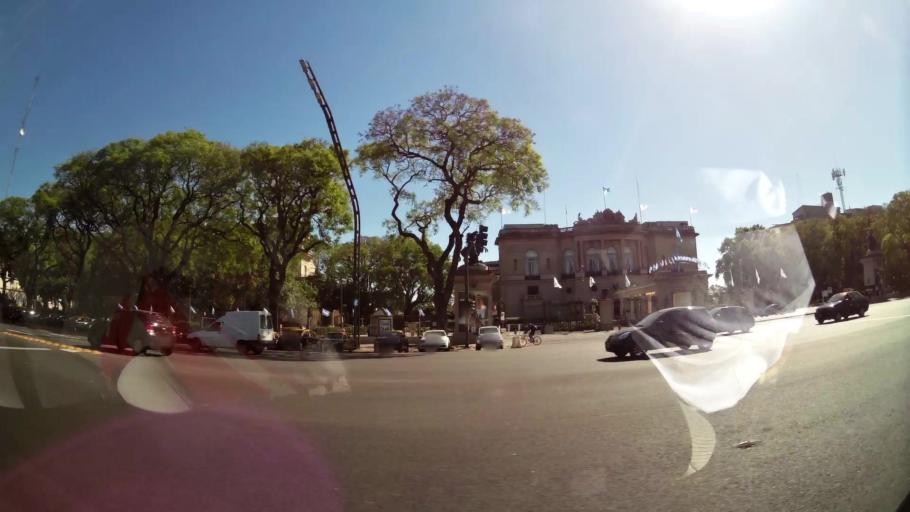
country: AR
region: Buenos Aires F.D.
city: Colegiales
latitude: -34.5695
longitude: -58.4267
